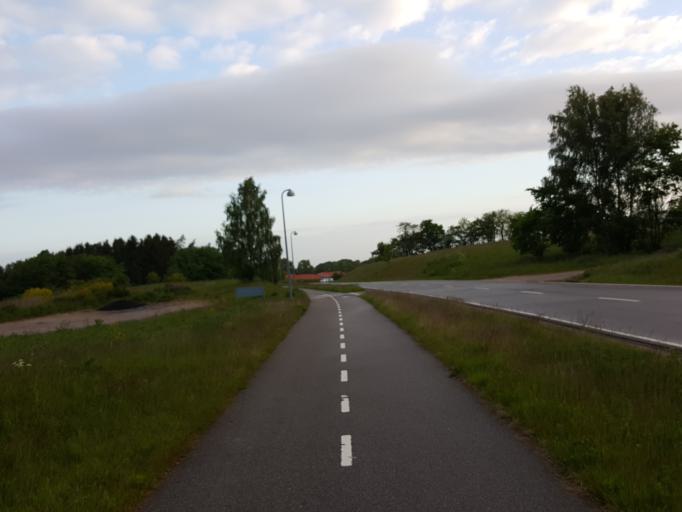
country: DK
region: Capital Region
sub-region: Rudersdal Kommune
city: Birkerod
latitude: 55.8510
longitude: 12.4577
